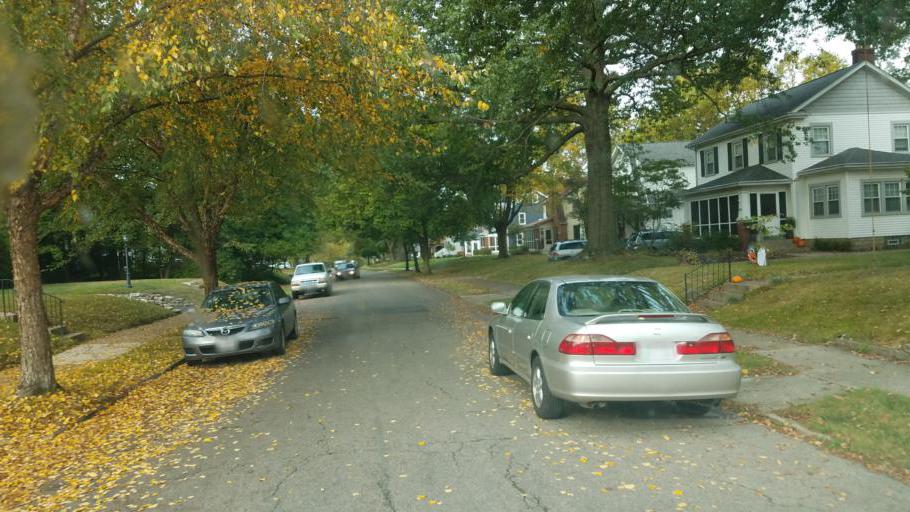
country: US
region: Ohio
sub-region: Franklin County
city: Worthington
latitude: 40.0360
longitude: -83.0050
